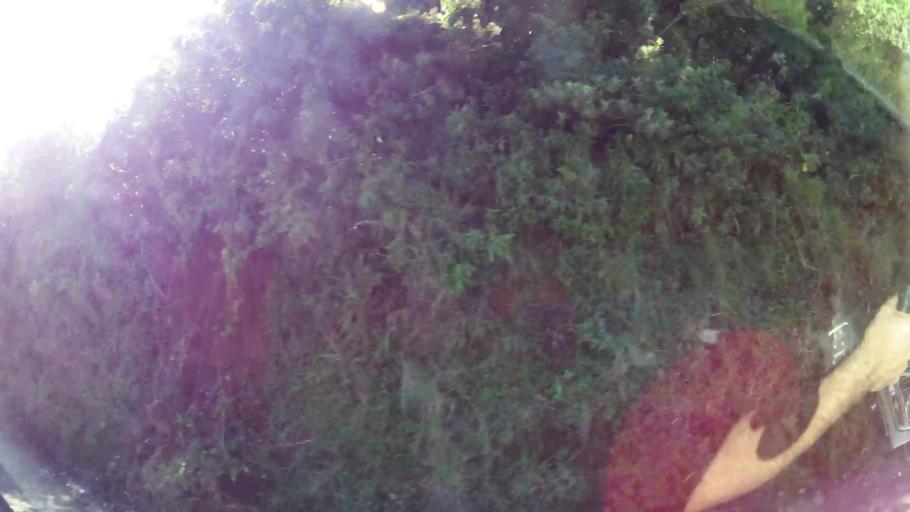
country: CR
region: Guanacaste
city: Juntas
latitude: 10.3319
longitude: -84.8510
